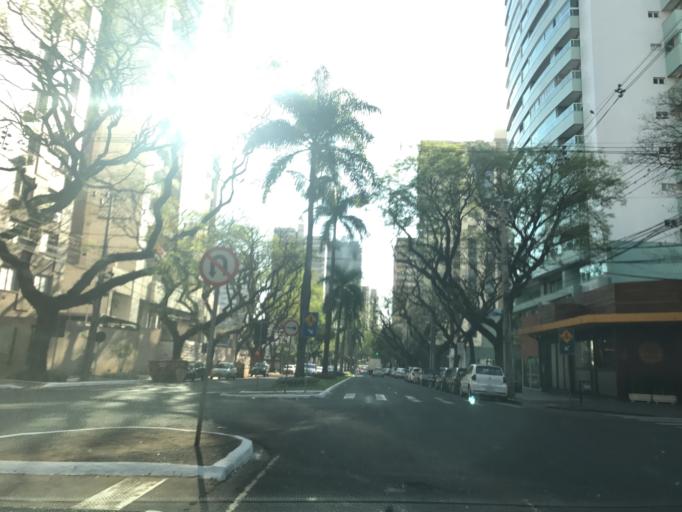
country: BR
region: Parana
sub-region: Maringa
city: Maringa
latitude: -23.4236
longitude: -51.9413
